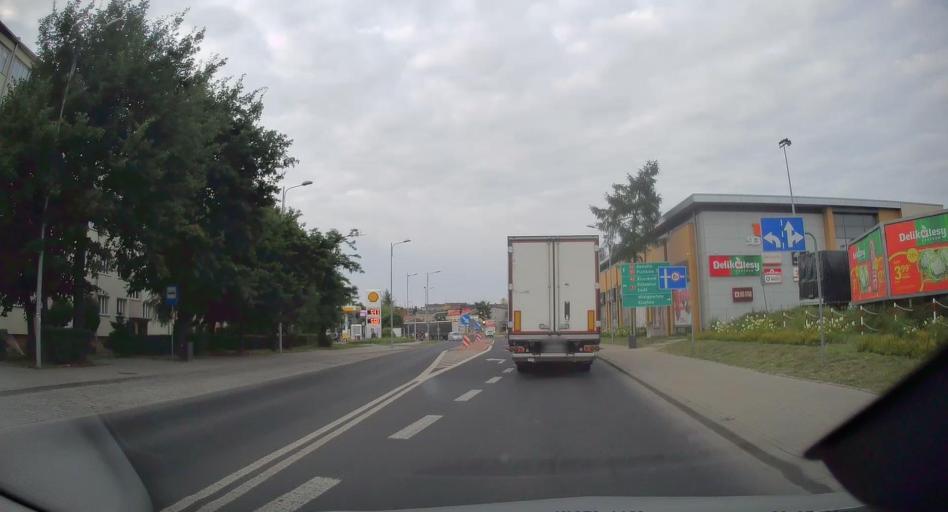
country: PL
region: Lodz Voivodeship
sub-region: Powiat radomszczanski
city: Radomsko
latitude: 51.0636
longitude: 19.4433
